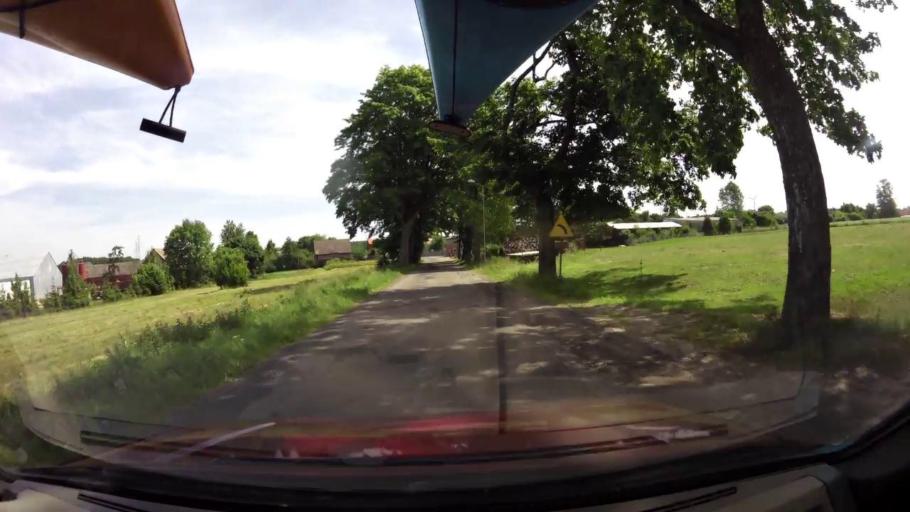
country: PL
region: West Pomeranian Voivodeship
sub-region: Powiat koszalinski
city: Sianow
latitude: 54.3224
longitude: 16.3464
